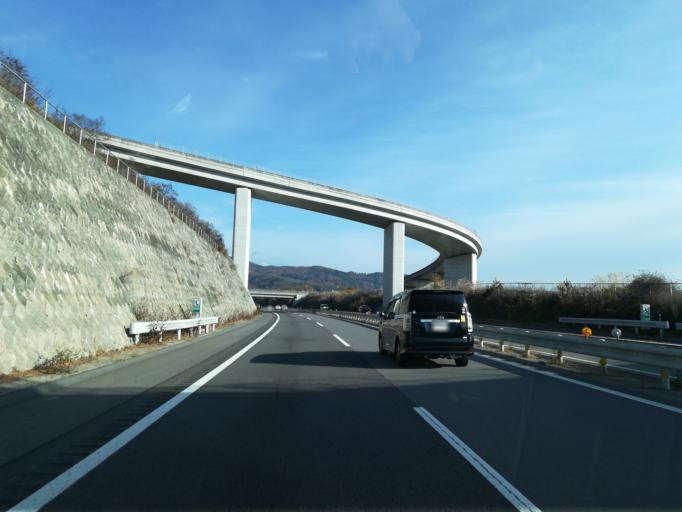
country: JP
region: Nagano
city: Ueda
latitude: 36.4097
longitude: 138.2909
